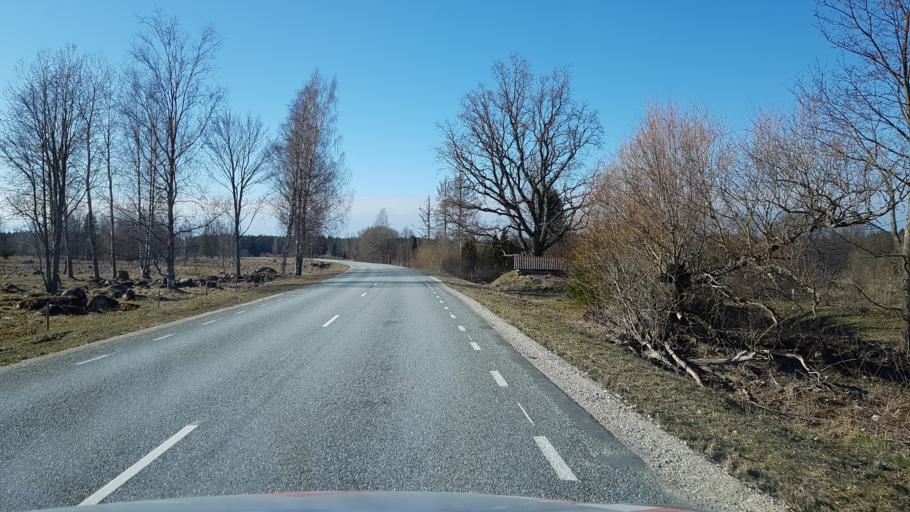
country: EE
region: Laeaene-Virumaa
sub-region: Kadrina vald
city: Kadrina
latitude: 59.5384
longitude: 26.0440
